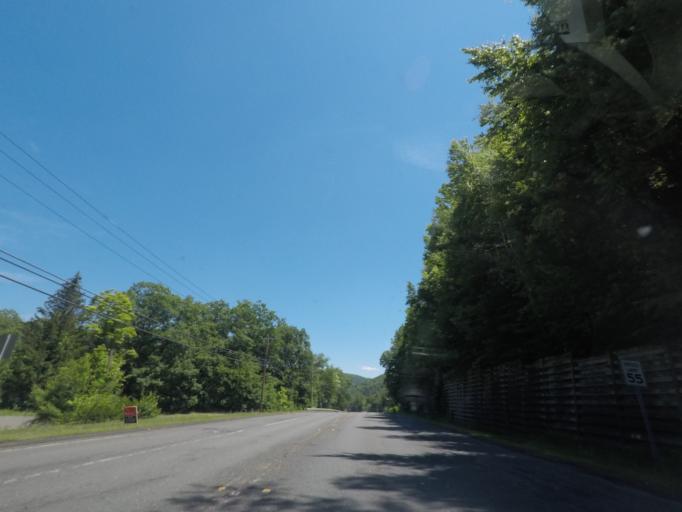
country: US
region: Massachusetts
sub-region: Hampden County
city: Granville
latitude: 42.1846
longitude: -72.8538
